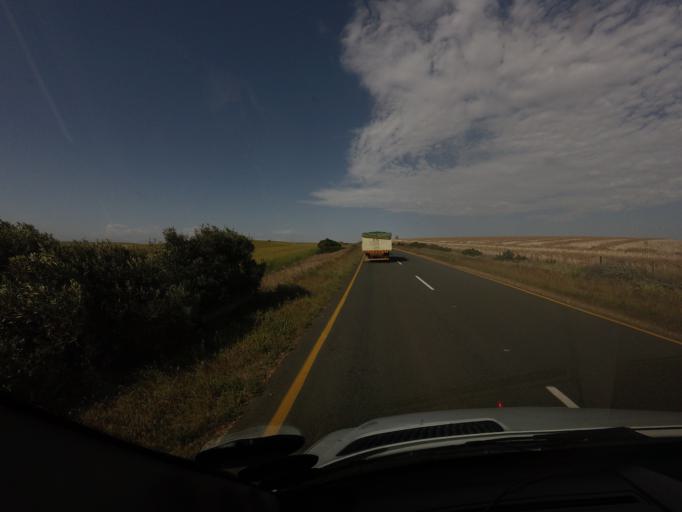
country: ZA
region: Western Cape
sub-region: Overberg District Municipality
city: Caledon
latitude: -34.3338
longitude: 19.7163
